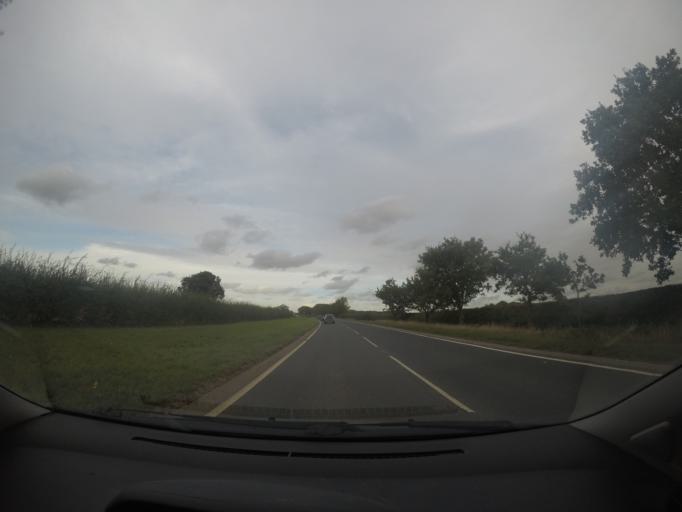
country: GB
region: England
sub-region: North Yorkshire
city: Riccall
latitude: 53.8580
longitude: -1.0496
